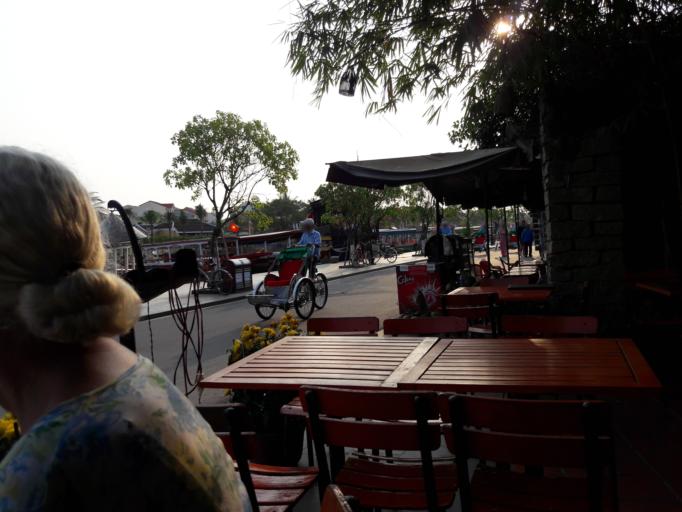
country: VN
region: Quang Nam
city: Hoi An
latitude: 15.8760
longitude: 108.3294
